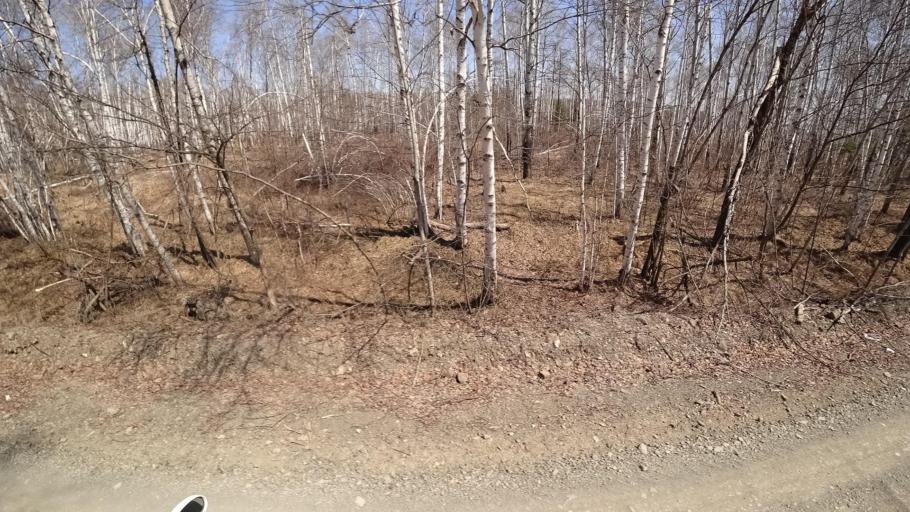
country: RU
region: Khabarovsk Krai
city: Khurba
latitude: 50.4174
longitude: 136.8368
